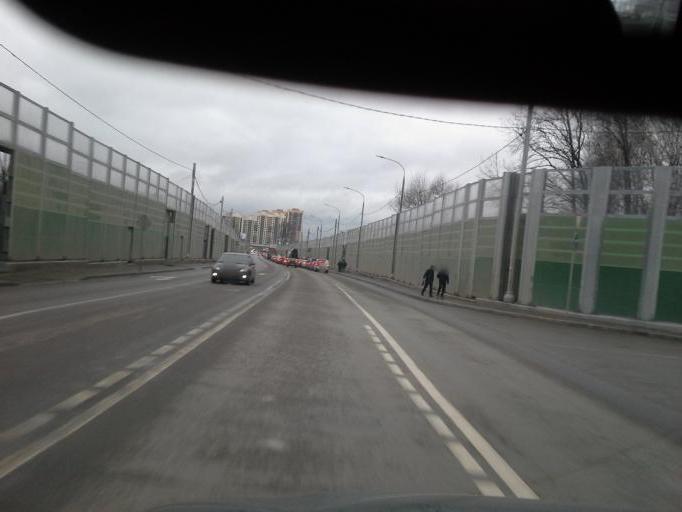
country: RU
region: Moscow
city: Novo-Peredelkino
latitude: 55.6271
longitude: 37.3374
